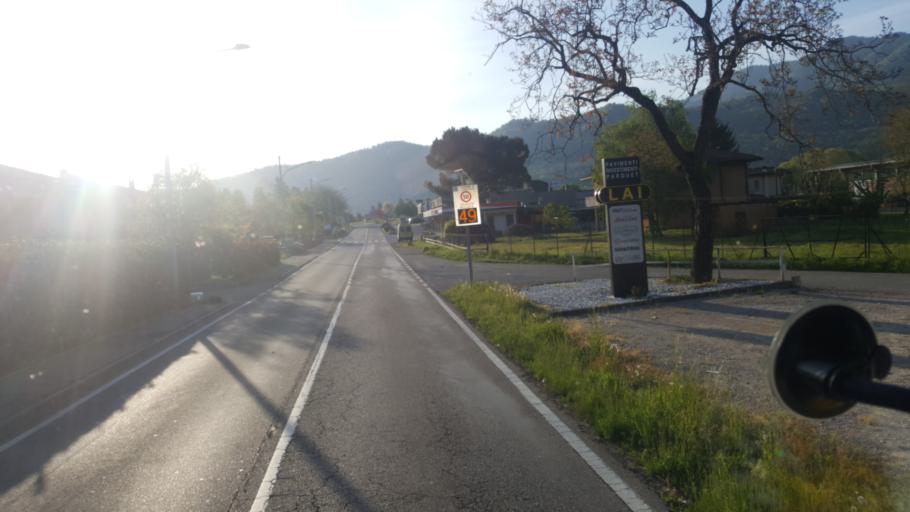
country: IT
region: Lombardy
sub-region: Provincia di Varese
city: Cuveglio
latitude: 45.9061
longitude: 8.7236
